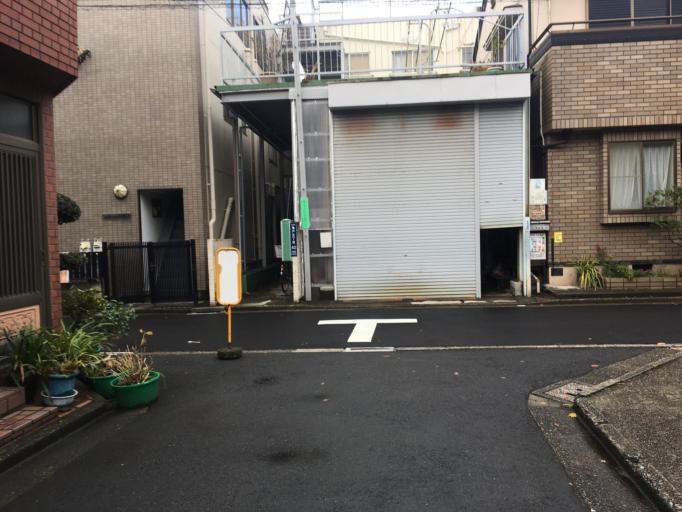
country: JP
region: Tokyo
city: Urayasu
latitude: 35.6997
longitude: 139.8322
